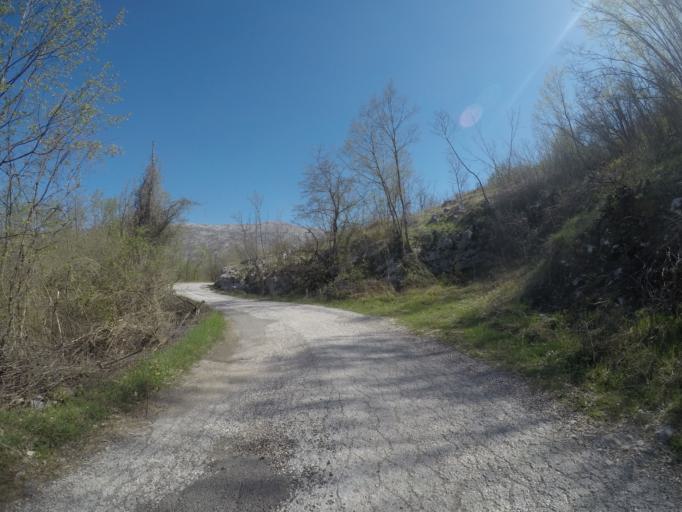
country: ME
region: Danilovgrad
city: Danilovgrad
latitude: 42.5369
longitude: 18.9916
